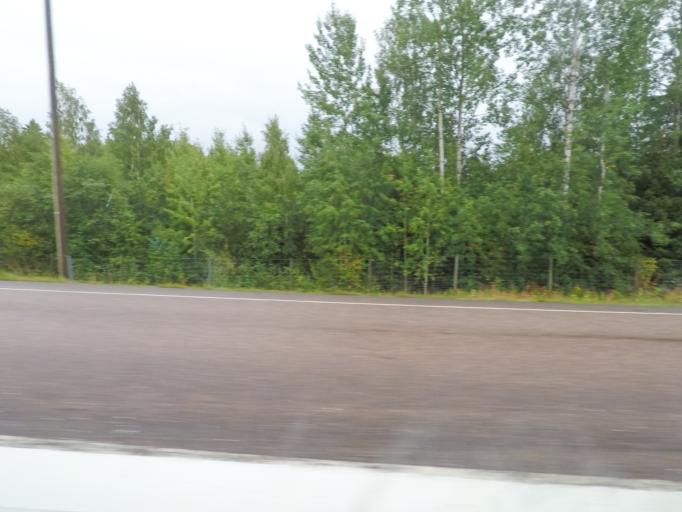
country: FI
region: Northern Savo
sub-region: Varkaus
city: Varkaus
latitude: 62.2576
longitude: 27.8736
